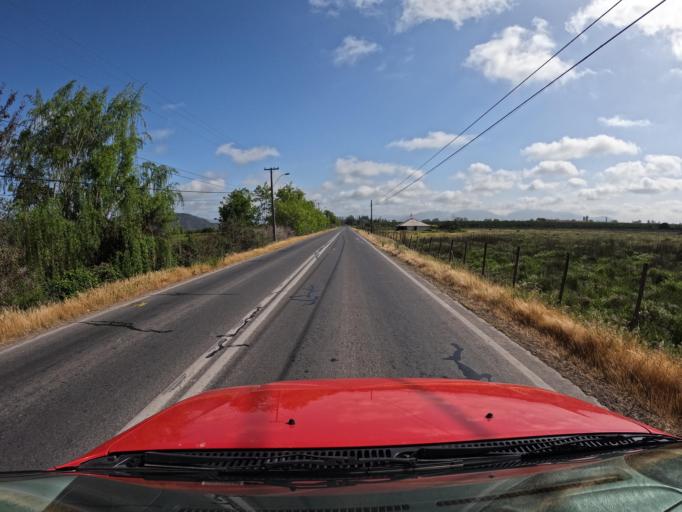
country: CL
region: Maule
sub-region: Provincia de Curico
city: Rauco
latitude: -34.9148
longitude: -71.2774
